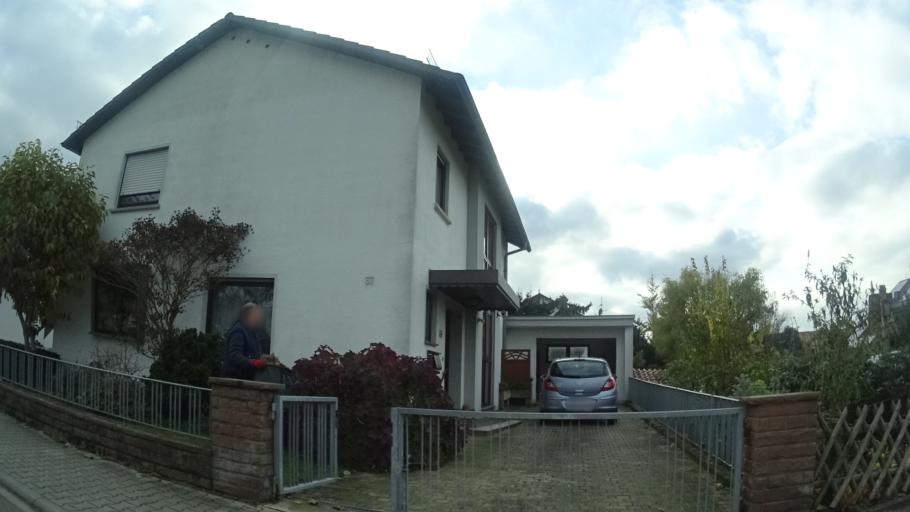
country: DE
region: Baden-Wuerttemberg
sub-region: Karlsruhe Region
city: Weinheim
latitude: 49.5325
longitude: 8.6484
